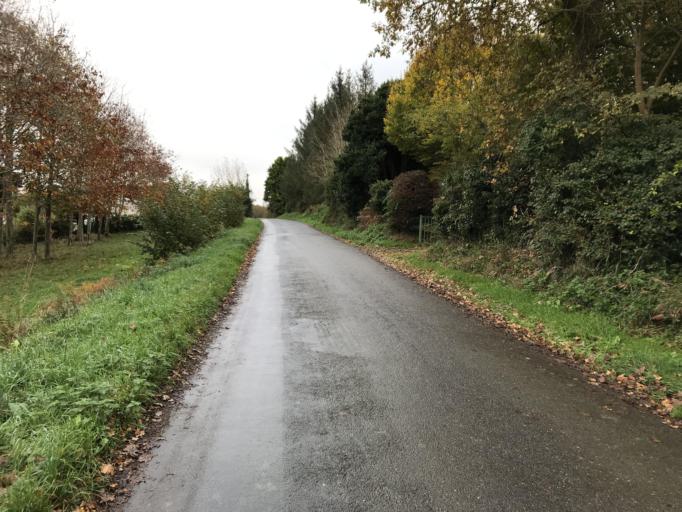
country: FR
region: Brittany
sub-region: Departement du Finistere
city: Logonna-Daoulas
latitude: 48.3346
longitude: -4.3133
